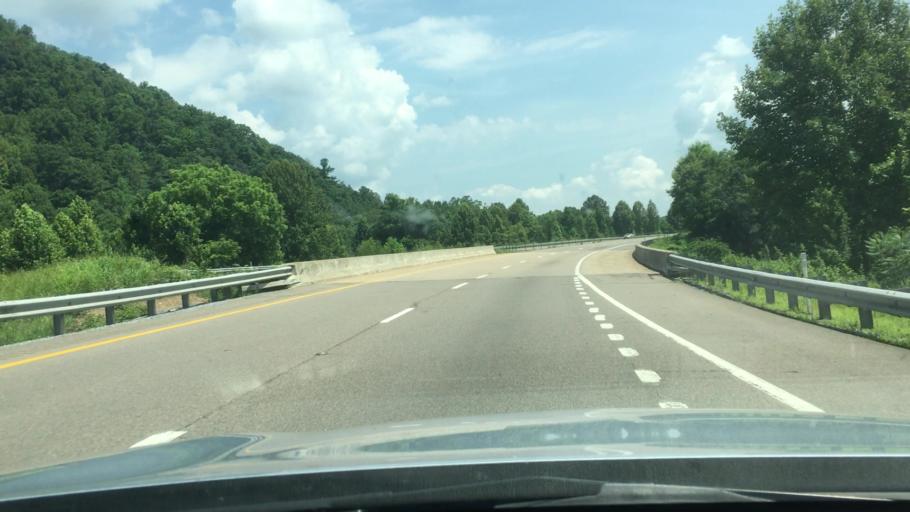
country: US
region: Tennessee
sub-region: Unicoi County
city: Erwin
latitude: 36.1697
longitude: -82.3939
